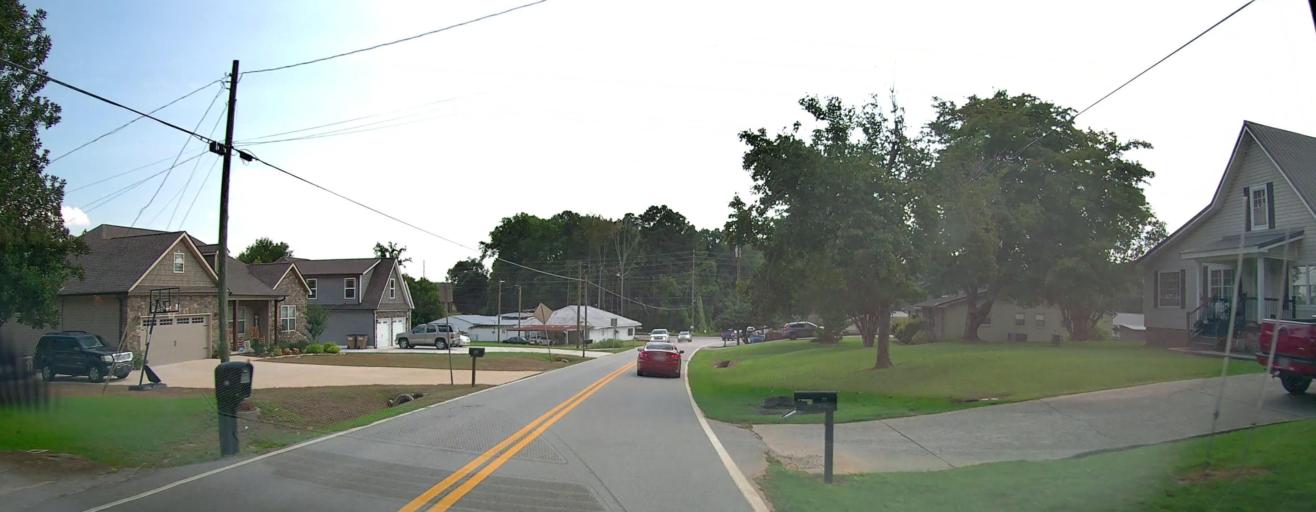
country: US
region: Georgia
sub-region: Catoosa County
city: Ringgold
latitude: 34.9130
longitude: -85.0866
